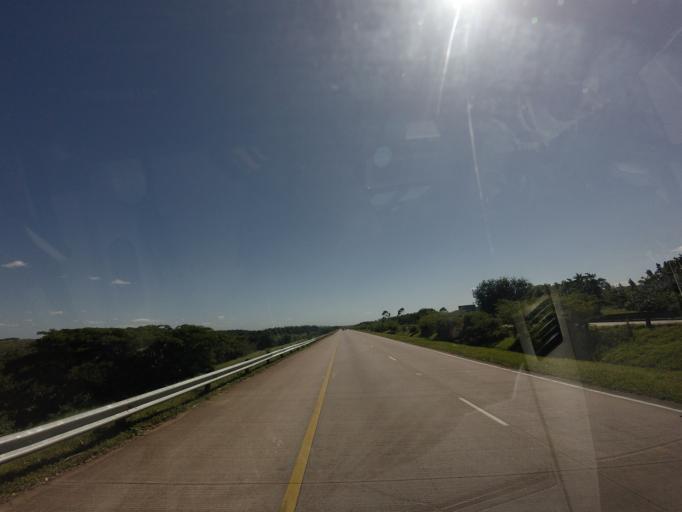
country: ZA
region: KwaZulu-Natal
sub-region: iLembe District Municipality
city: Ballitoville
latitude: -29.4709
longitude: 31.2345
